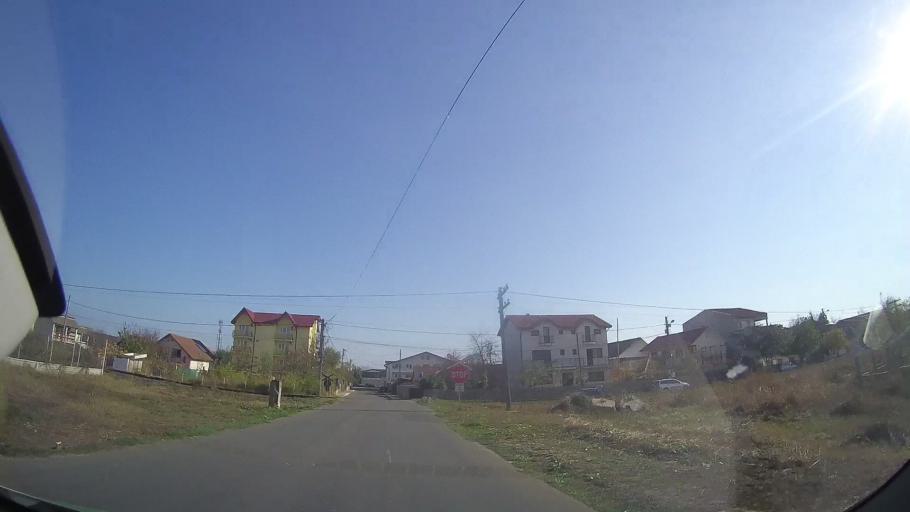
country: RO
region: Constanta
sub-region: Comuna Costinesti
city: Costinesti
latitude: 43.9537
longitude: 28.6324
